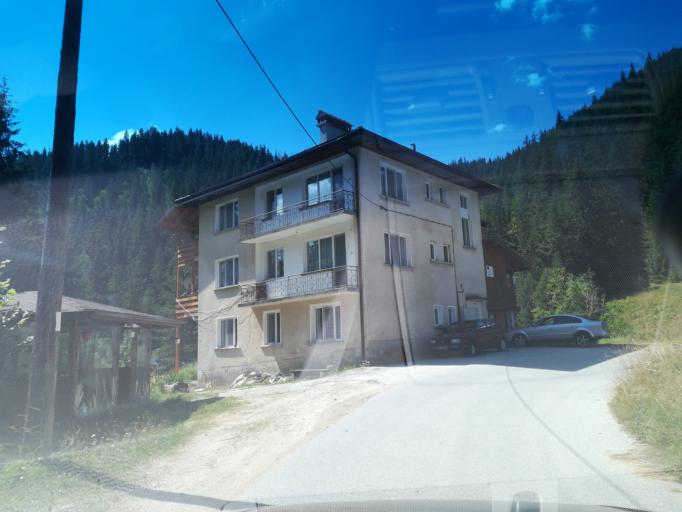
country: BG
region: Smolyan
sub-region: Obshtina Smolyan
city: Smolyan
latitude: 41.6587
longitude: 24.8182
